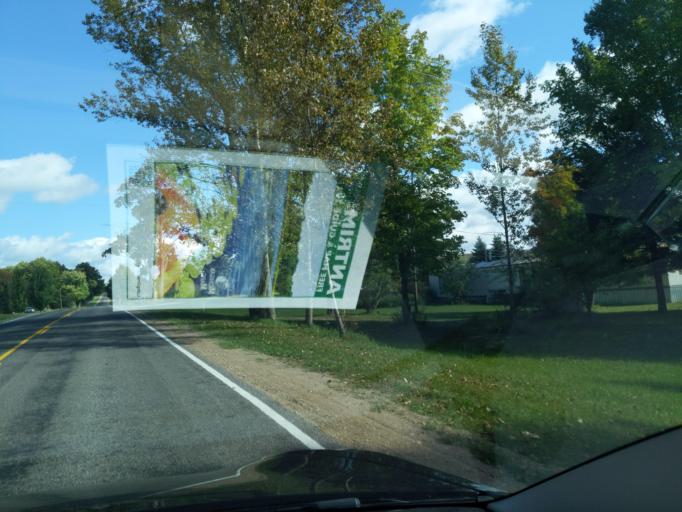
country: US
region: Michigan
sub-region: Antrim County
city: Elk Rapids
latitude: 44.9353
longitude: -85.3617
